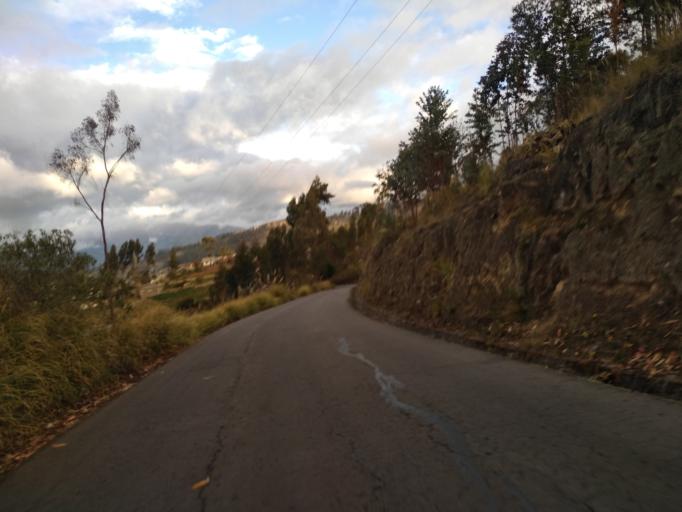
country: EC
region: Chimborazo
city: Riobamba
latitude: -1.7041
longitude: -78.7048
